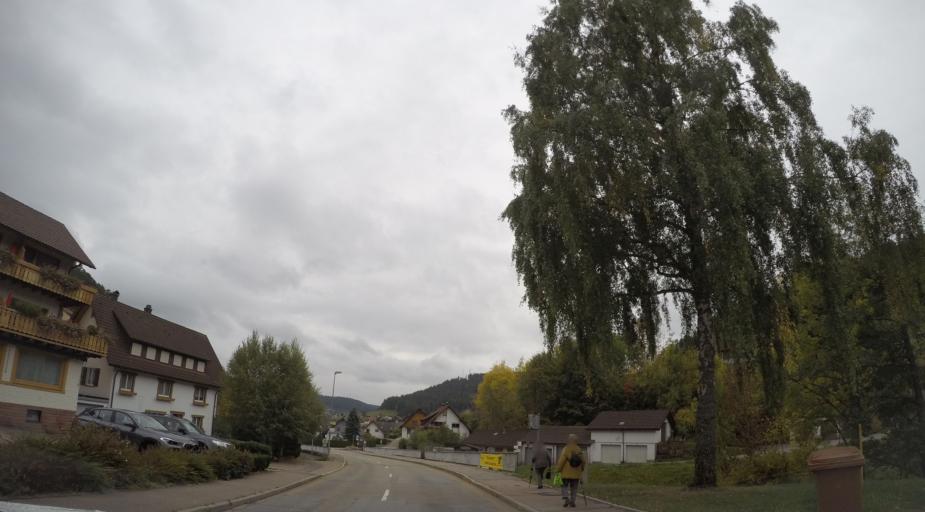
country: DE
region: Baden-Wuerttemberg
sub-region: Karlsruhe Region
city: Baiersbronn
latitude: 48.5297
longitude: 8.3617
